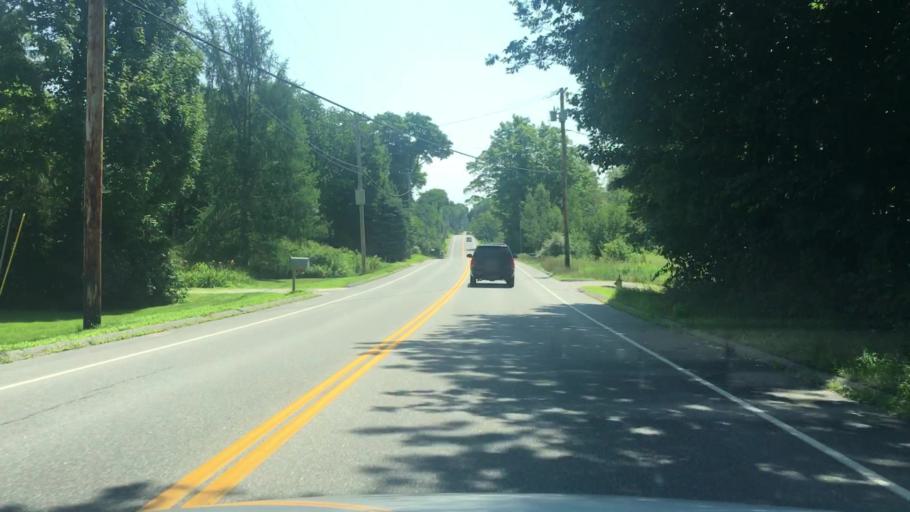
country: US
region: Maine
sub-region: Cumberland County
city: Cumberland Center
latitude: 43.8066
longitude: -70.2788
